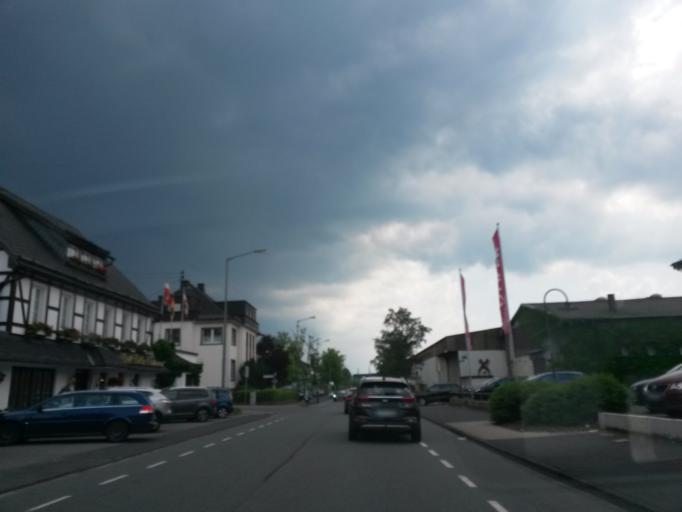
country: DE
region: North Rhine-Westphalia
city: Kreuztal
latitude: 50.9561
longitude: 7.9943
